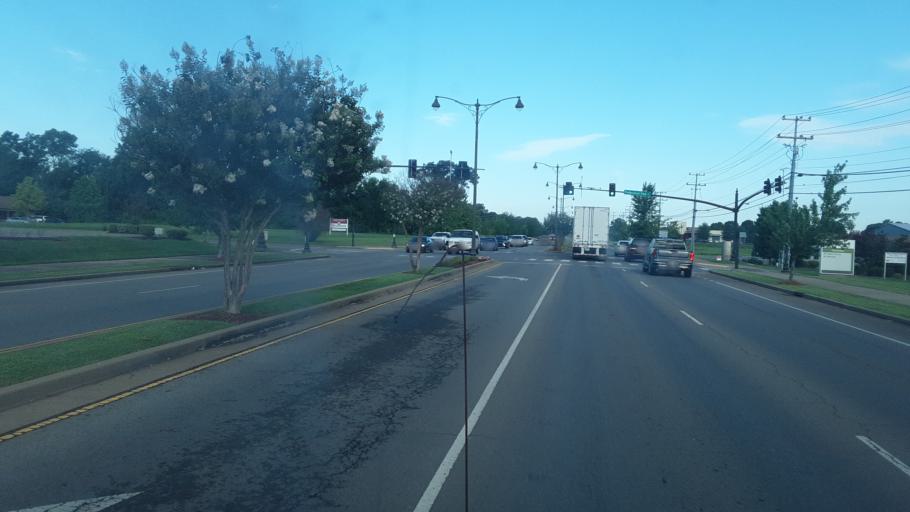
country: US
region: Tennessee
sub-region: Montgomery County
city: Clarksville
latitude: 36.5799
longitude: -87.2712
